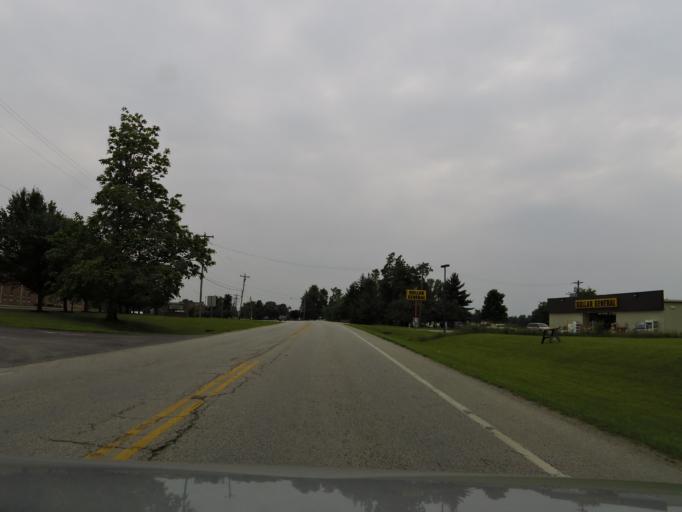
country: US
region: Ohio
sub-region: Clinton County
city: Blanchester
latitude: 39.1830
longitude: -83.9325
